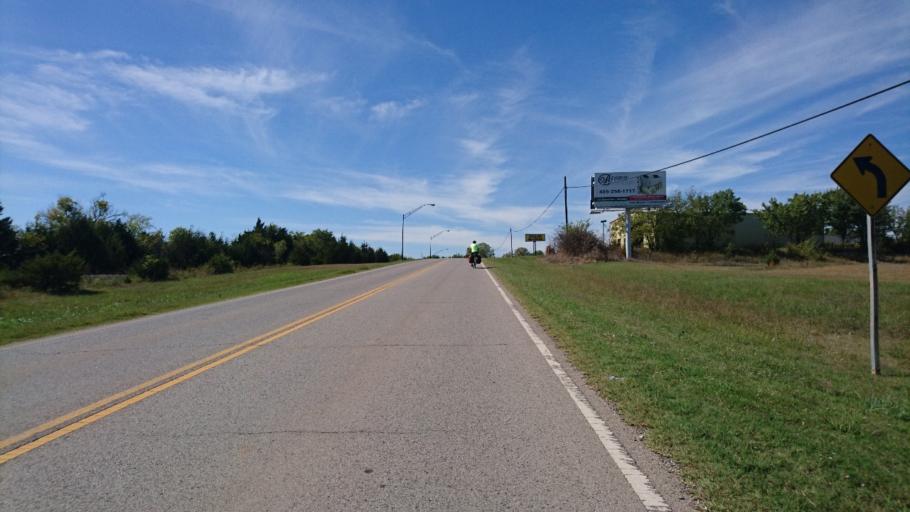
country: US
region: Oklahoma
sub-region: Lincoln County
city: Stroud
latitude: 35.7506
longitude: -96.6704
